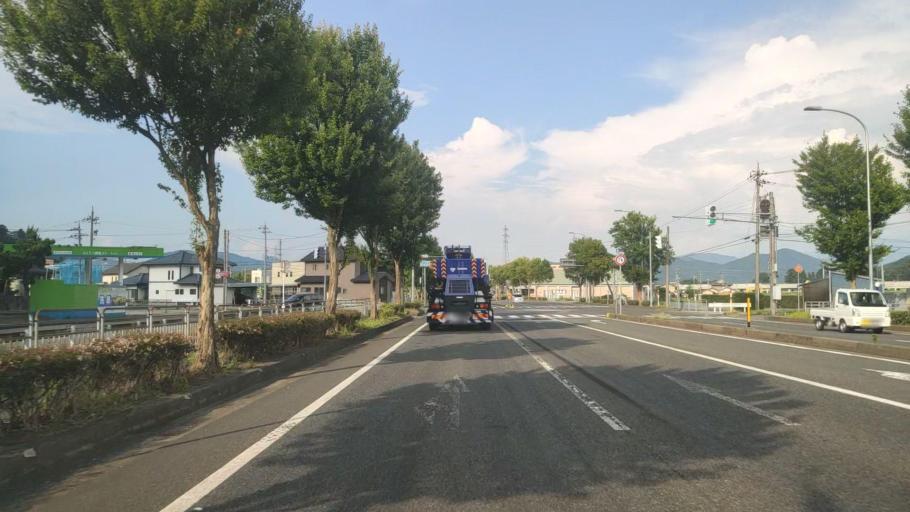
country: JP
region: Fukui
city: Takefu
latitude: 35.8871
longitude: 136.1888
